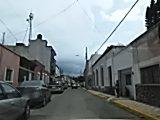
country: MX
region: Nayarit
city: Tepic
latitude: 21.5078
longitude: -104.8968
